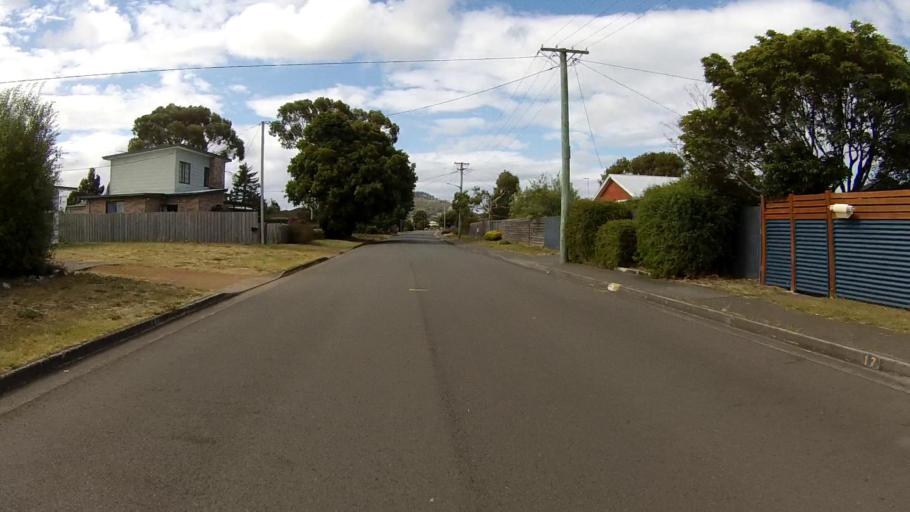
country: AU
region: Tasmania
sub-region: Clarence
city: Lauderdale
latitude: -42.9034
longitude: 147.4925
